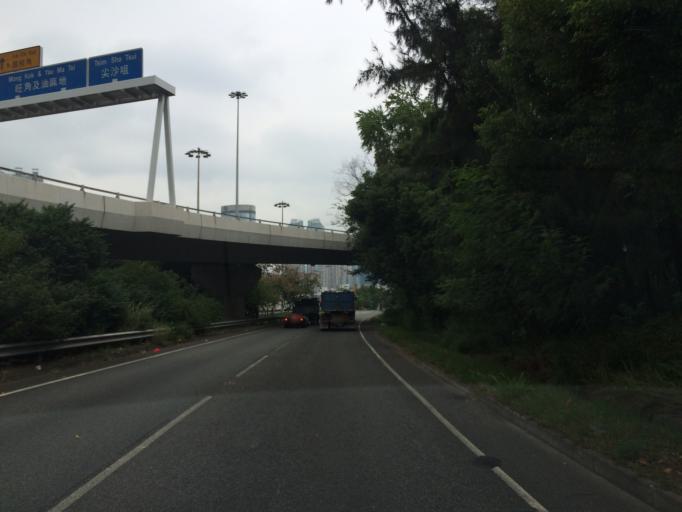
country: HK
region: Sham Shui Po
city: Sham Shui Po
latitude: 22.3112
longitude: 114.1608
